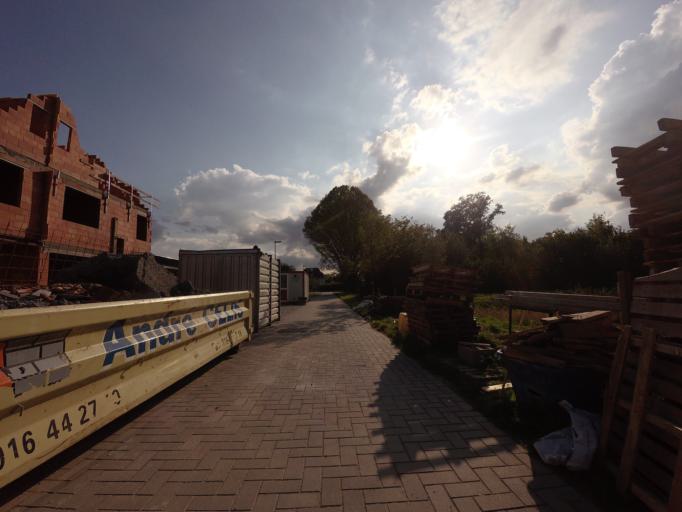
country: BE
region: Flanders
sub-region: Provincie Vlaams-Brabant
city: Boortmeerbeek
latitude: 50.9787
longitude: 4.5614
